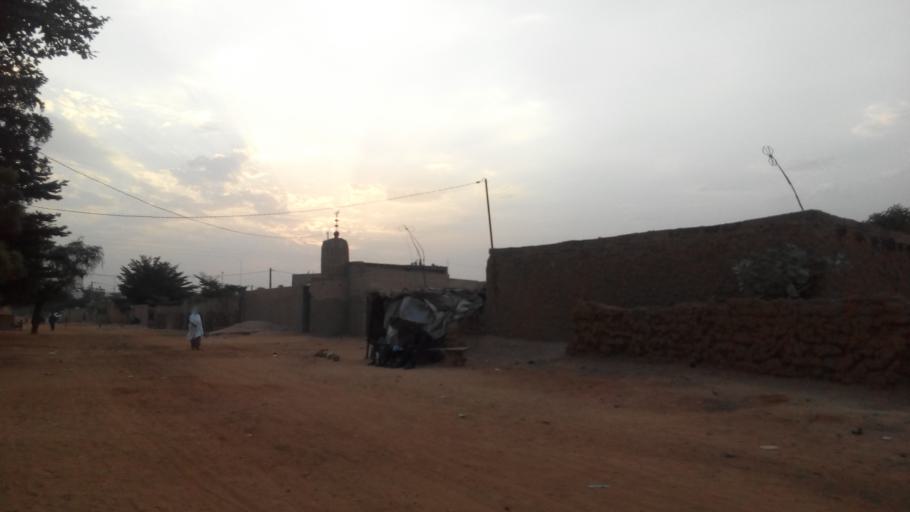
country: NE
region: Niamey
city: Niamey
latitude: 13.5431
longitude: 2.0417
